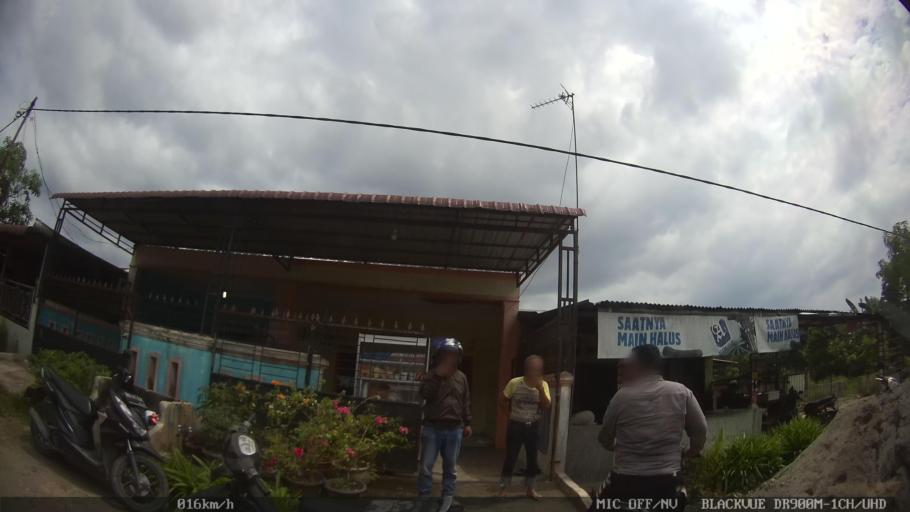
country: ID
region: North Sumatra
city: Sunggal
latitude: 3.6237
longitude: 98.6032
